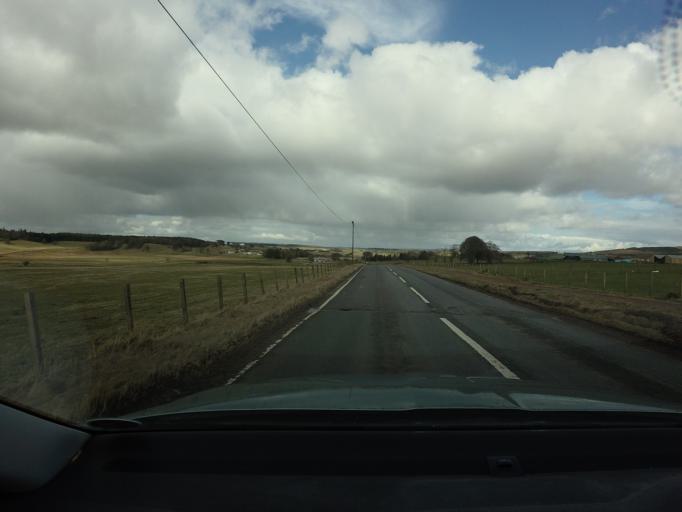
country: GB
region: Scotland
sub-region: South Lanarkshire
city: Lanark
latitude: 55.6473
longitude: -3.7336
